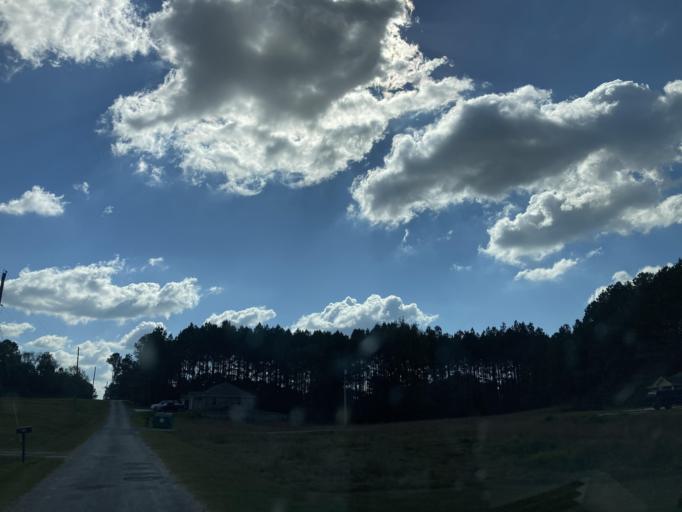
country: US
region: Mississippi
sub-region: Lamar County
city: Sumrall
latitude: 31.3862
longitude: -89.5400
